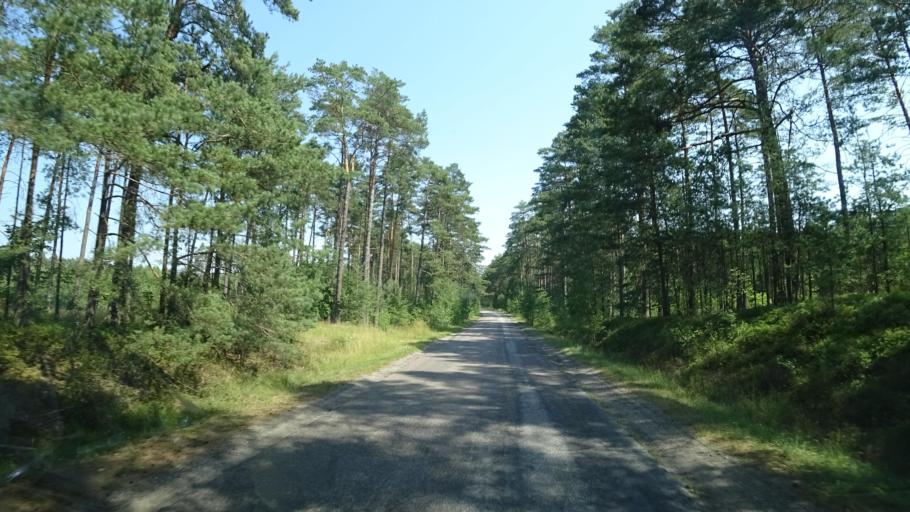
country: PL
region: Pomeranian Voivodeship
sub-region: Powiat chojnicki
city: Brusy
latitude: 53.8676
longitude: 17.6164
